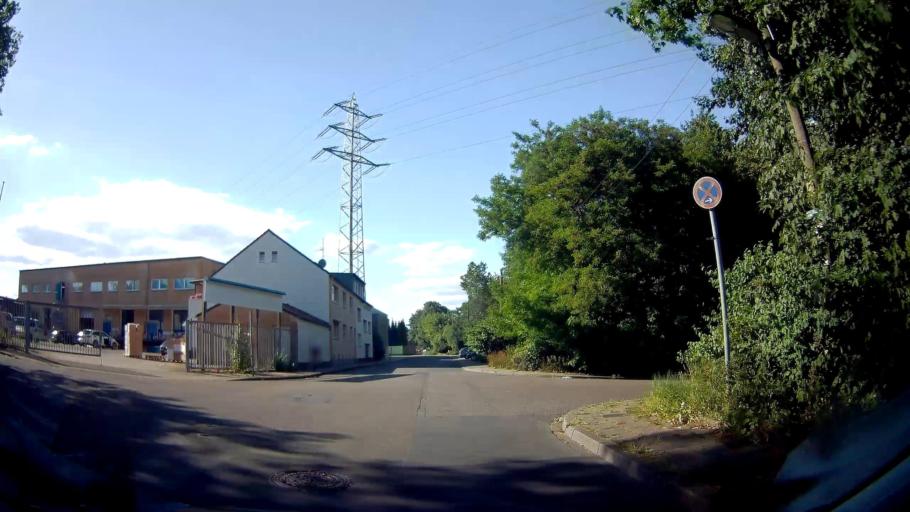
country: DE
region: North Rhine-Westphalia
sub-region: Regierungsbezirk Dusseldorf
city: Essen
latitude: 51.4691
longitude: 7.0061
